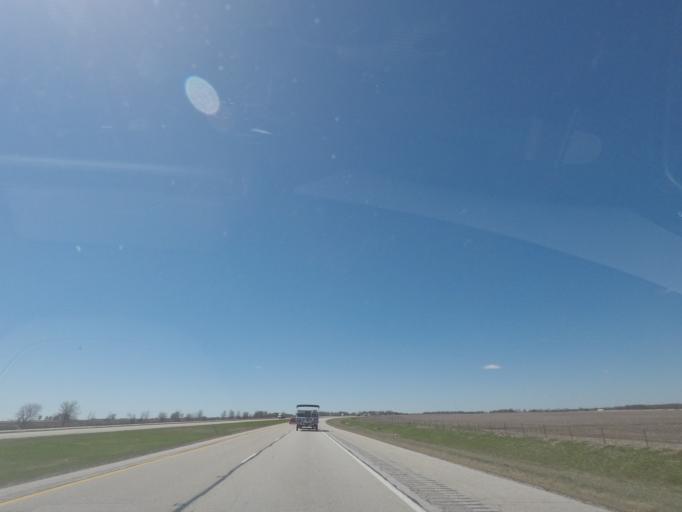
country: US
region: Illinois
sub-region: McLean County
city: Lexington
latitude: 40.5922
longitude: -88.8580
